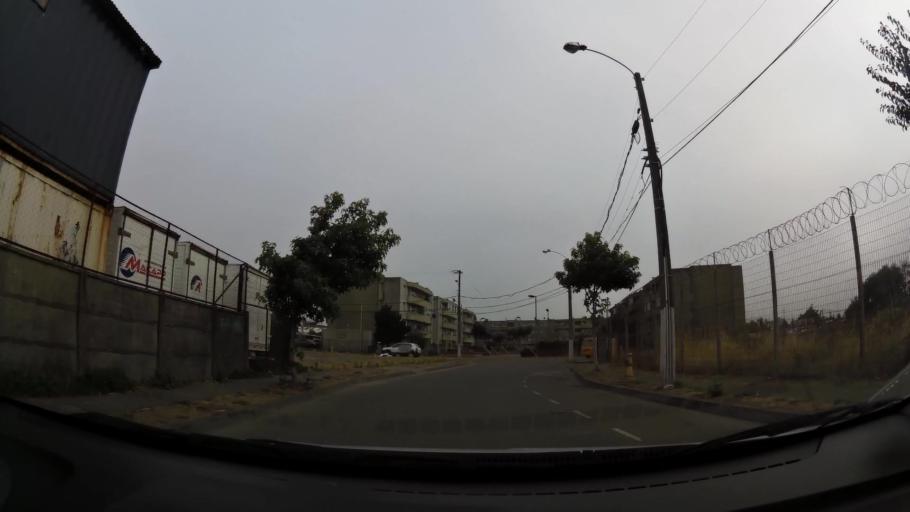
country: CL
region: Biobio
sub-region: Provincia de Concepcion
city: Concepcion
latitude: -36.7956
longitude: -73.0852
